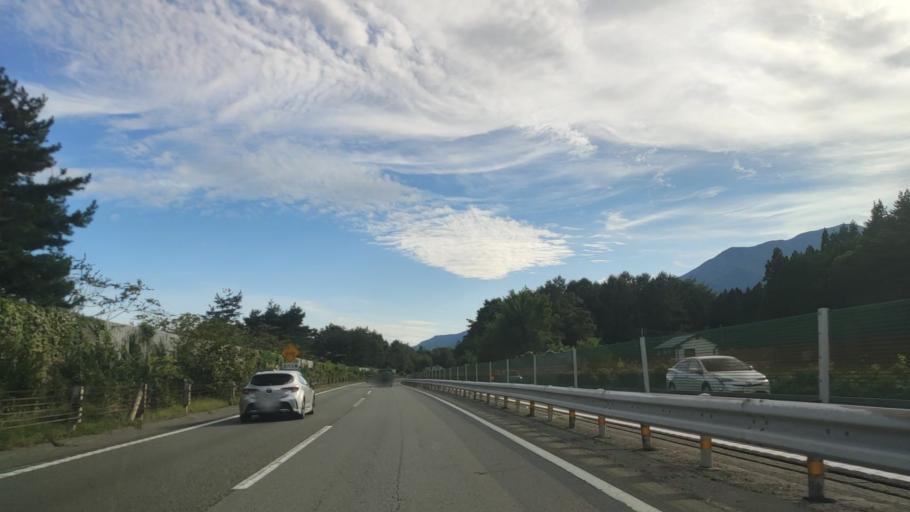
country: JP
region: Nagano
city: Ina
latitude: 35.7588
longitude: 137.9172
